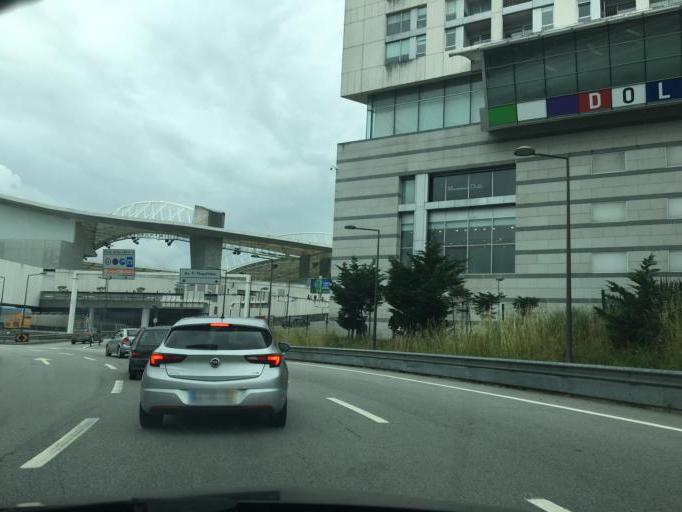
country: PT
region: Porto
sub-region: Maia
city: Pedroucos
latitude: 41.1642
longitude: -8.5824
